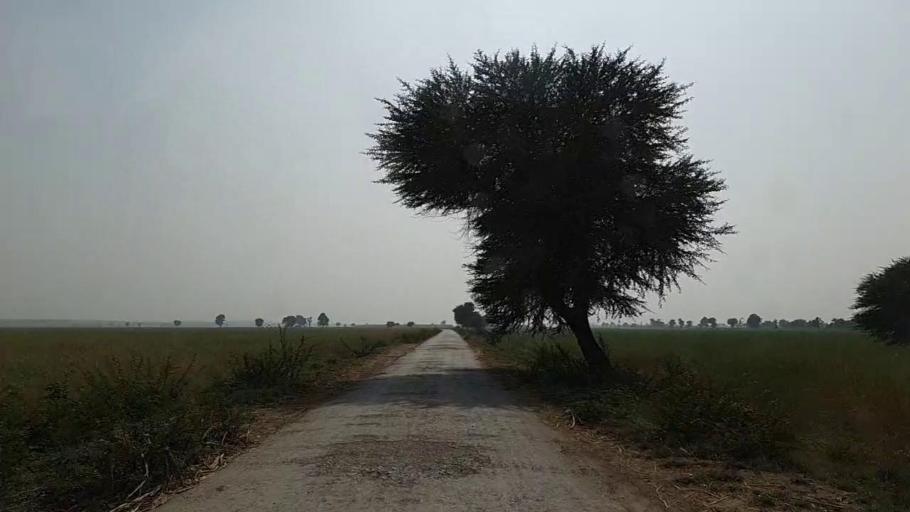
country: PK
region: Sindh
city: Naukot
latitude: 24.7664
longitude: 69.3491
